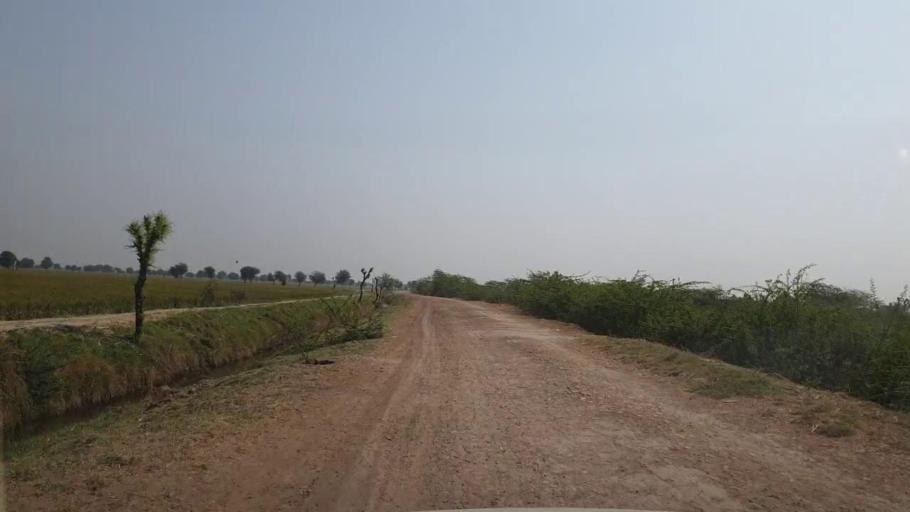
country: PK
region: Sindh
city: Dhoro Naro
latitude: 25.4596
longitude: 69.6699
